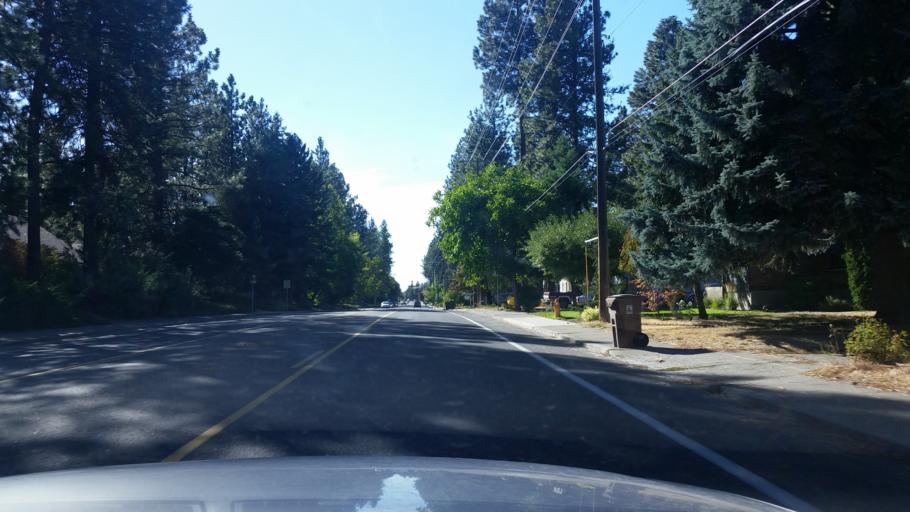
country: US
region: Washington
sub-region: Spokane County
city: Spokane
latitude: 47.6283
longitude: -117.4184
